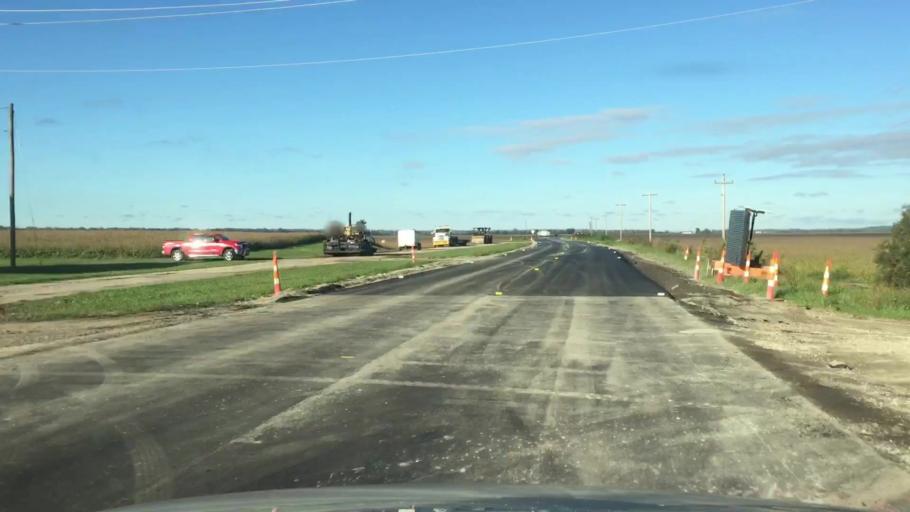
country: US
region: Missouri
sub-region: Howard County
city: New Franklin
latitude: 38.9917
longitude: -92.6200
